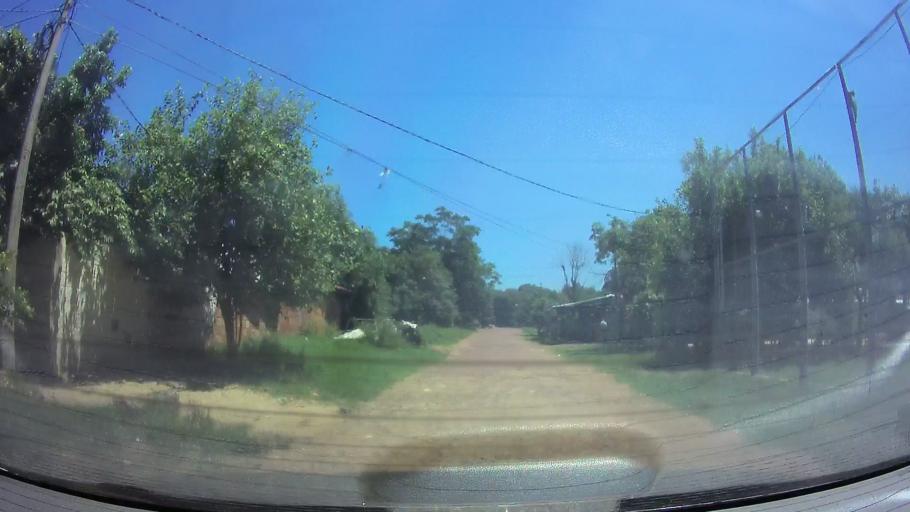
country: PY
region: Central
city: San Lorenzo
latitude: -25.3127
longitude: -57.4913
